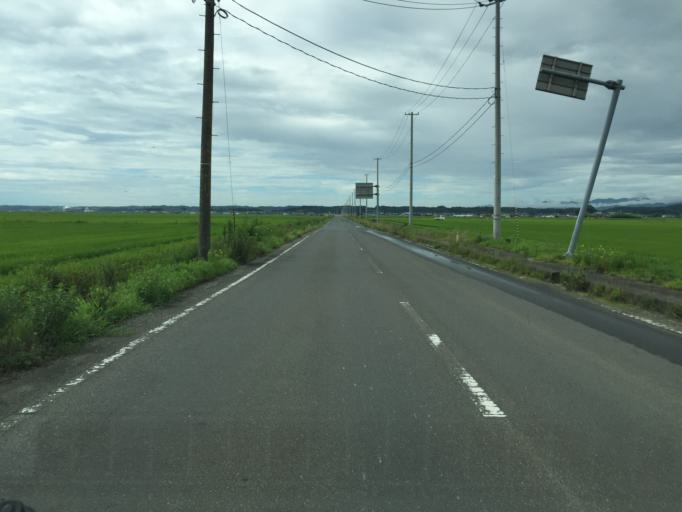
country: JP
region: Miyagi
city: Marumori
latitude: 37.8035
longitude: 140.9566
